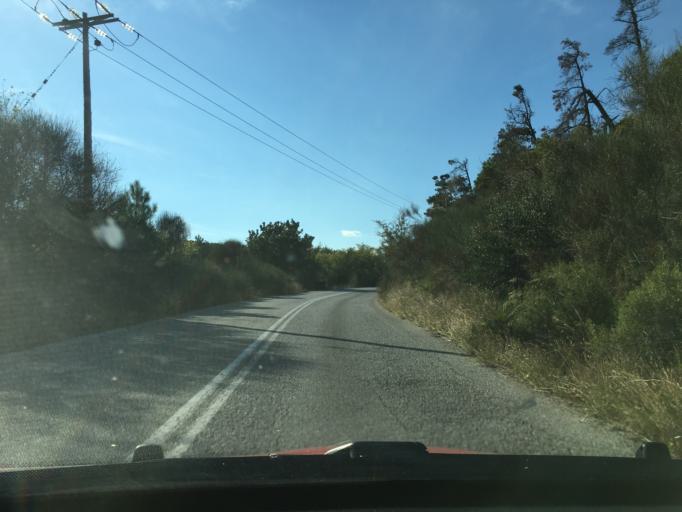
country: GR
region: Central Macedonia
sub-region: Nomos Chalkidikis
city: Megali Panagia
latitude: 40.3823
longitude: 23.7394
